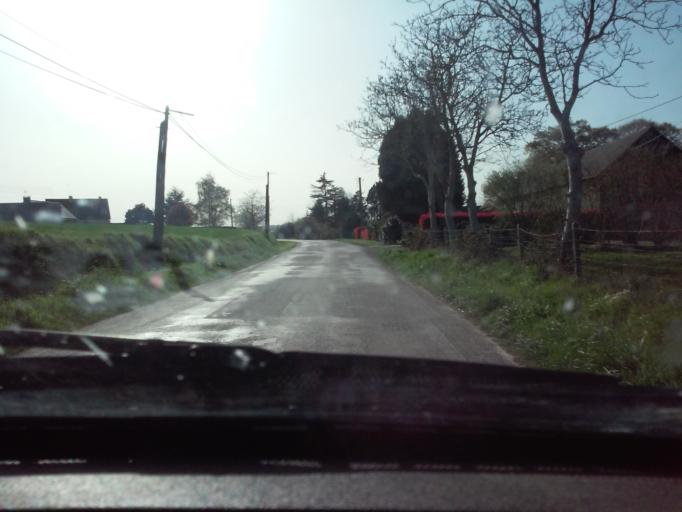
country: FR
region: Brittany
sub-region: Departement d'Ille-et-Vilaine
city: Javene
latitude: 48.3191
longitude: -1.2341
